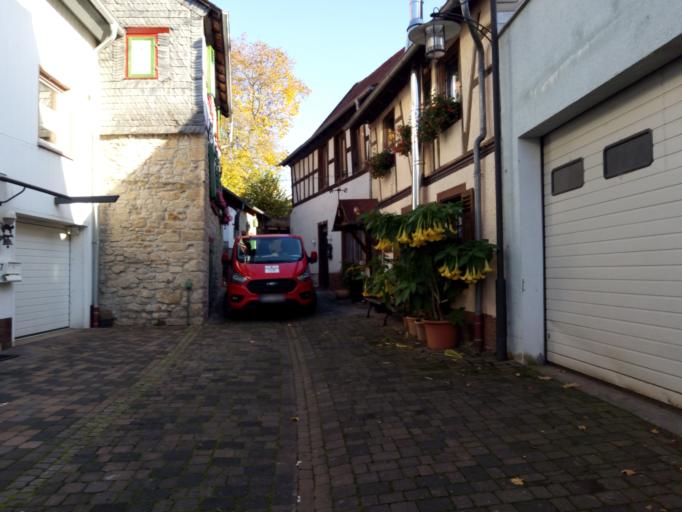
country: DE
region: Rheinland-Pfalz
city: Monzingen
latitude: 49.8006
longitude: 7.5917
